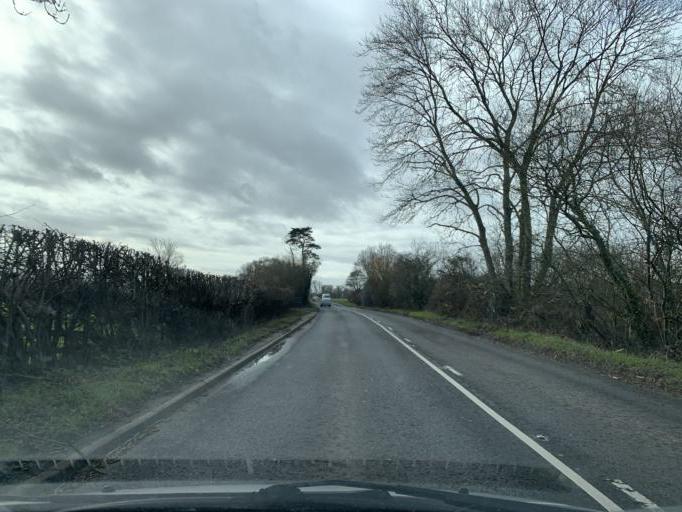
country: GB
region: England
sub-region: Wiltshire
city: Downton
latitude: 50.9834
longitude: -1.7614
